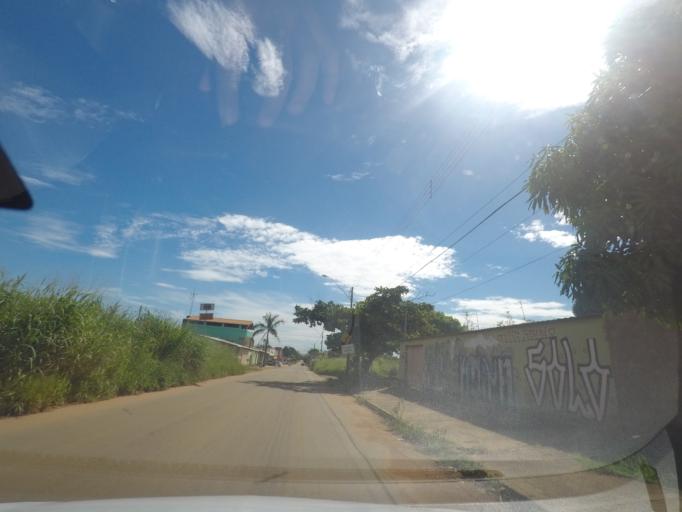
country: BR
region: Goias
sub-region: Aparecida De Goiania
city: Aparecida de Goiania
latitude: -16.8092
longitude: -49.2911
